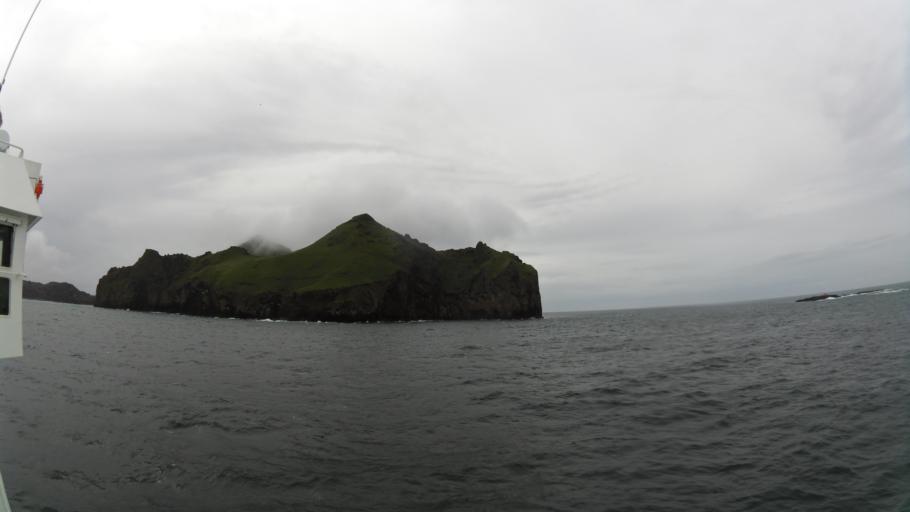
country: IS
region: South
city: Vestmannaeyjar
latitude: 63.4536
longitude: -20.2301
